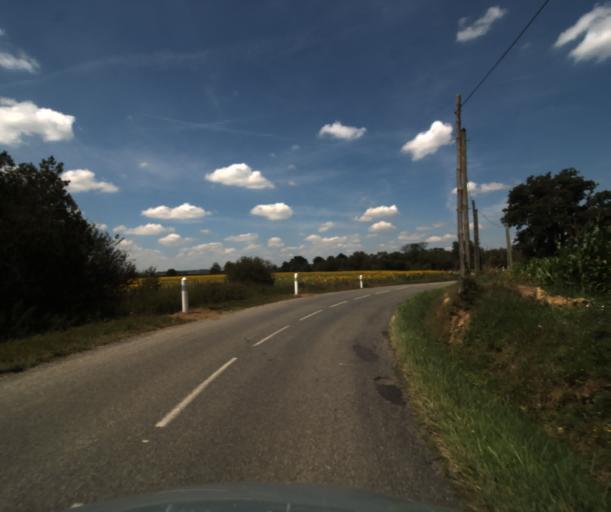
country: FR
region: Midi-Pyrenees
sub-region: Departement de la Haute-Garonne
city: Saint-Lys
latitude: 43.4919
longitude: 1.1794
